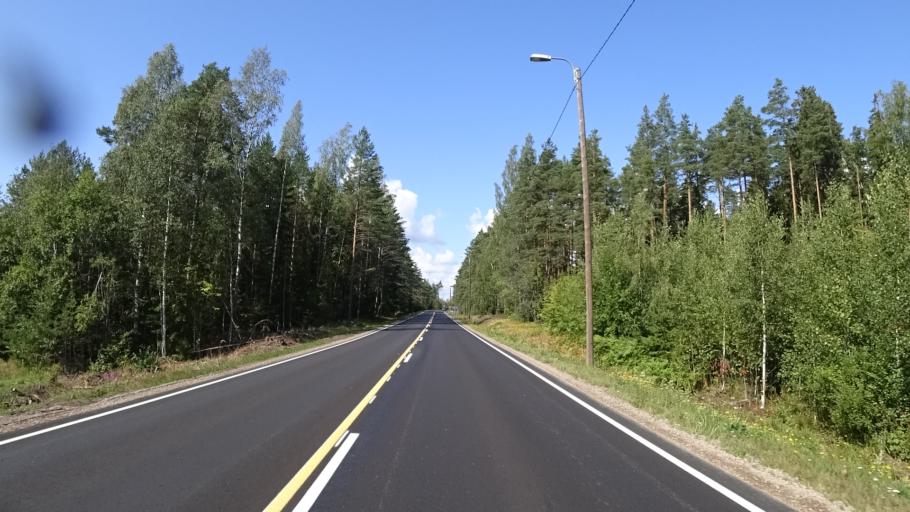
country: FI
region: Kymenlaakso
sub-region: Kotka-Hamina
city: Karhula
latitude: 60.5526
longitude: 26.9050
